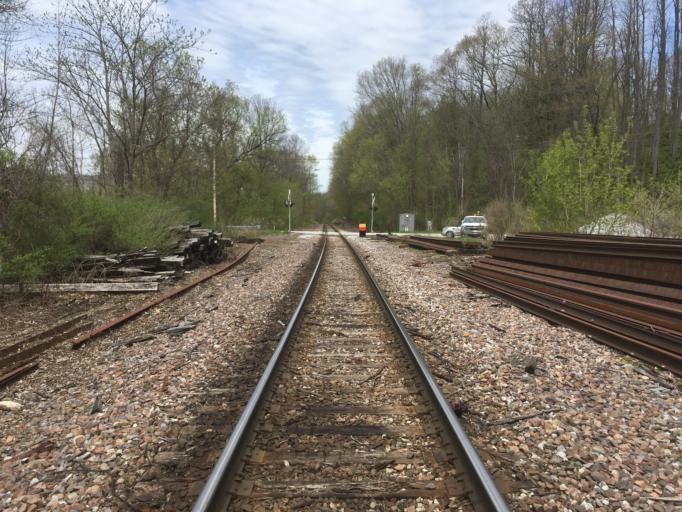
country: US
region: Vermont
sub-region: Rutland County
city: Brandon
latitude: 43.7110
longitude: -73.0382
